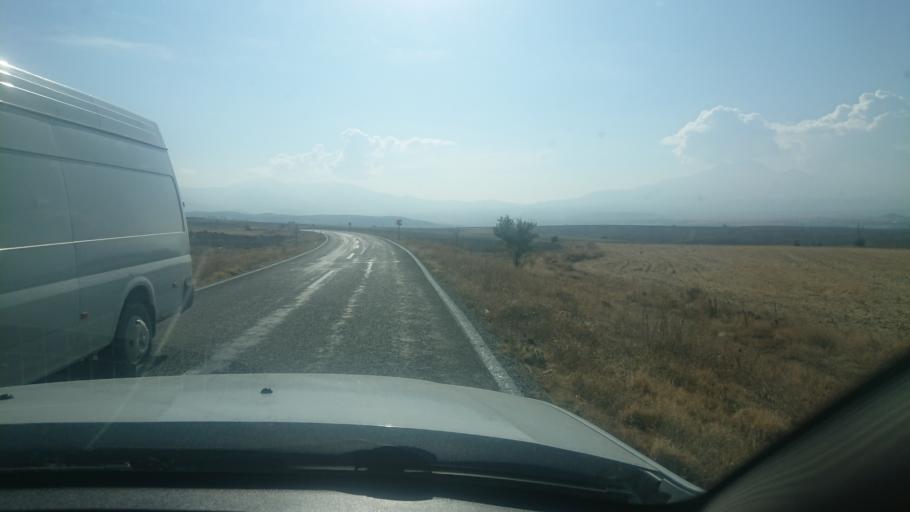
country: TR
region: Aksaray
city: Guzelyurt
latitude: 38.2611
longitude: 34.3314
